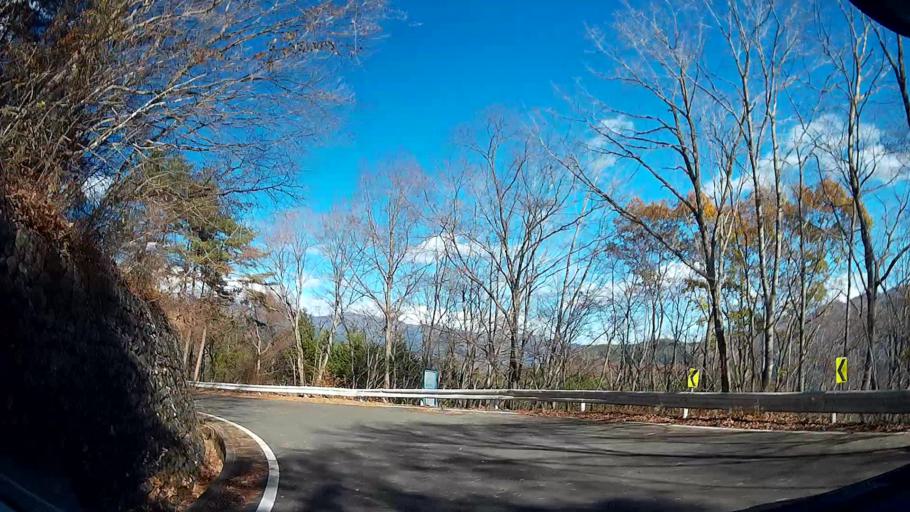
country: JP
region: Yamanashi
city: Otsuki
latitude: 35.7389
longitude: 138.9533
